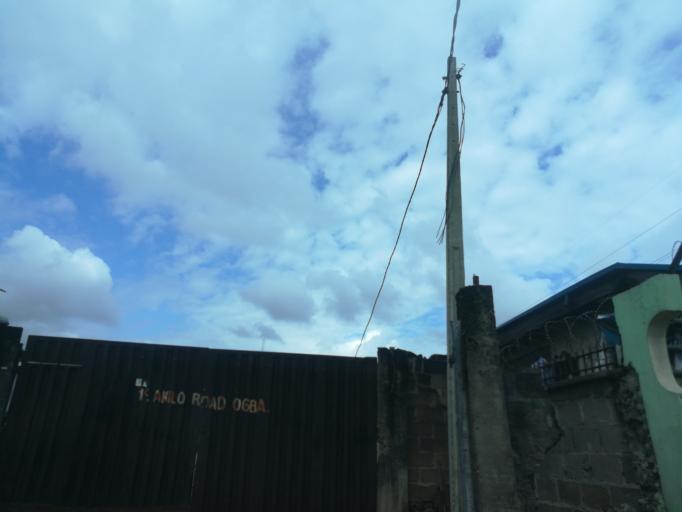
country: NG
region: Lagos
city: Agege
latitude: 6.6175
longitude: 3.3368
